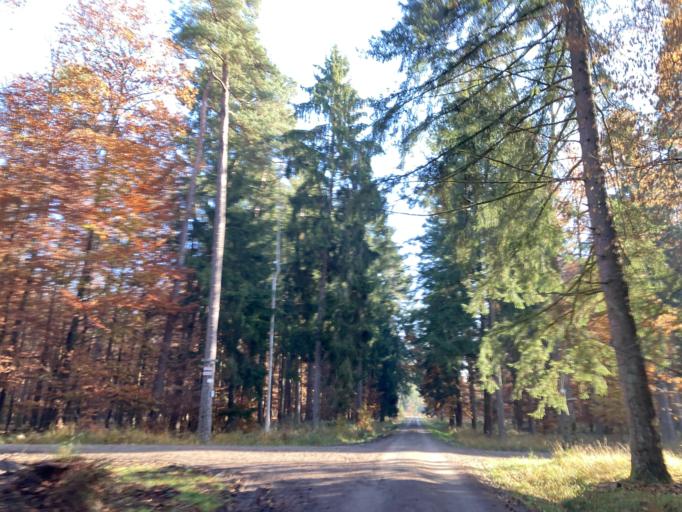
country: DE
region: Baden-Wuerttemberg
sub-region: Regierungsbezirk Stuttgart
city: Altdorf
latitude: 48.5758
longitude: 8.9943
